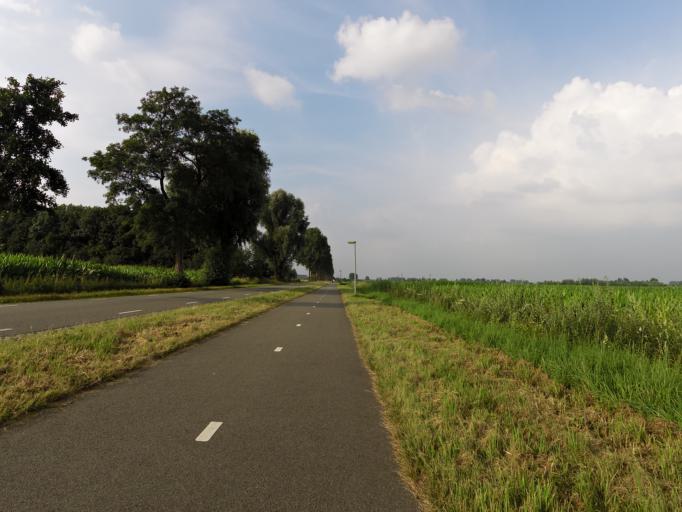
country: NL
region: Gelderland
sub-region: Gemeente Duiven
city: Duiven
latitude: 51.9641
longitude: 6.0324
